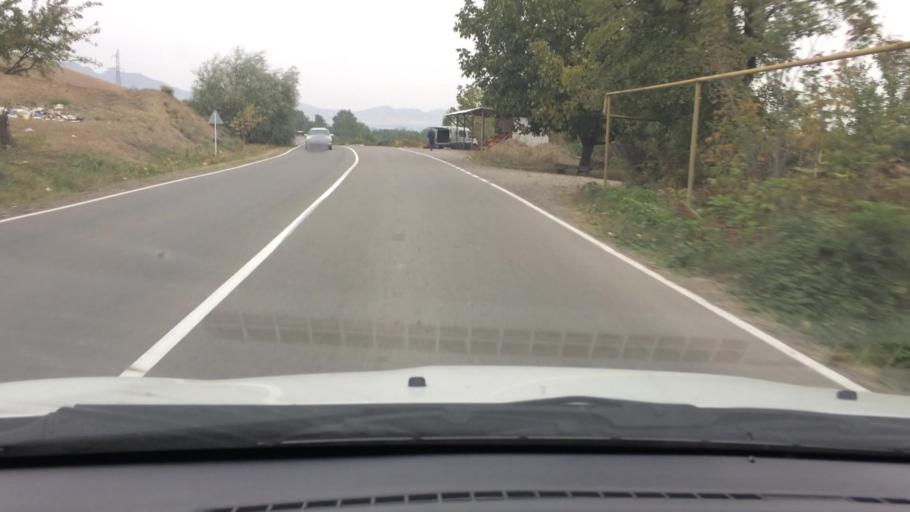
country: AM
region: Tavush
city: Bagratashen
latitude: 41.2812
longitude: 44.7909
